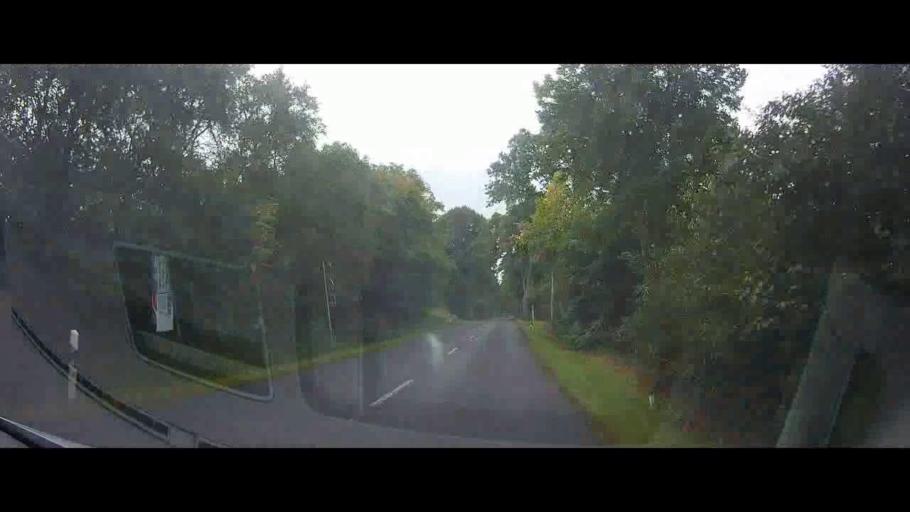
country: DE
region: Lower Saxony
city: Rosdorf
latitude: 51.5425
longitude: 9.8756
